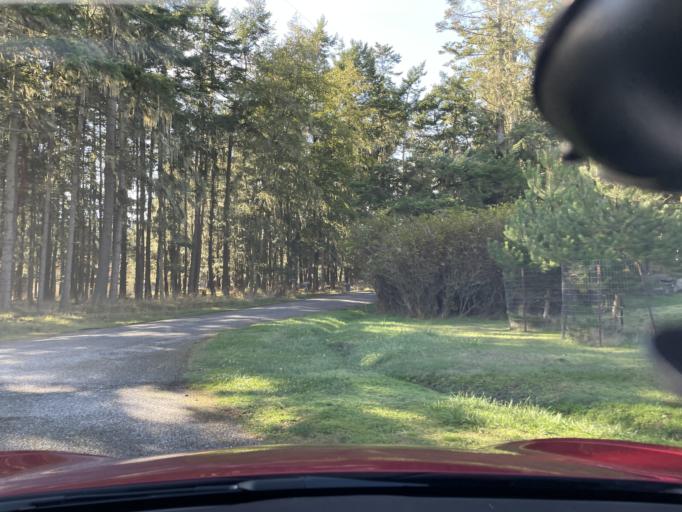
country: US
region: Washington
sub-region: San Juan County
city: Friday Harbor
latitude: 48.4612
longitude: -122.9635
